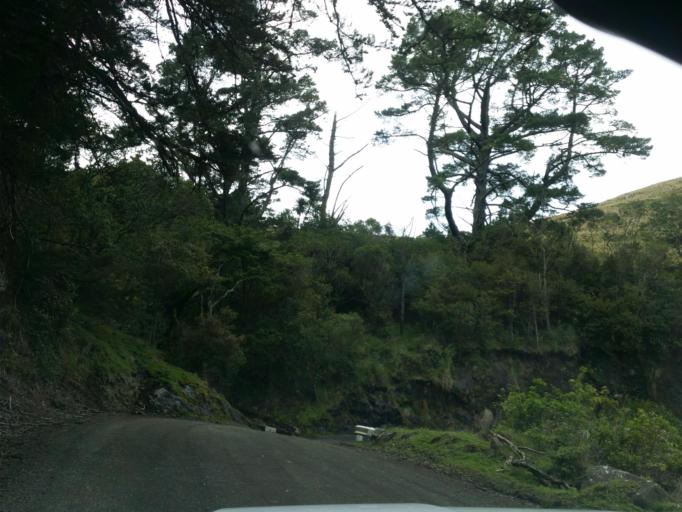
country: NZ
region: Northland
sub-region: Whangarei
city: Maungatapere
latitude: -35.8992
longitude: 174.1149
